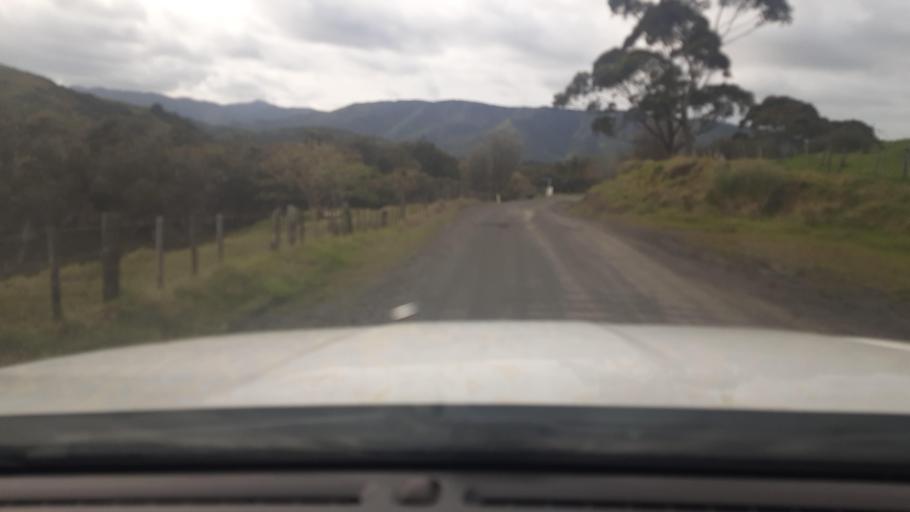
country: NZ
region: Northland
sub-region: Far North District
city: Ahipara
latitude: -35.3317
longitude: 173.2256
